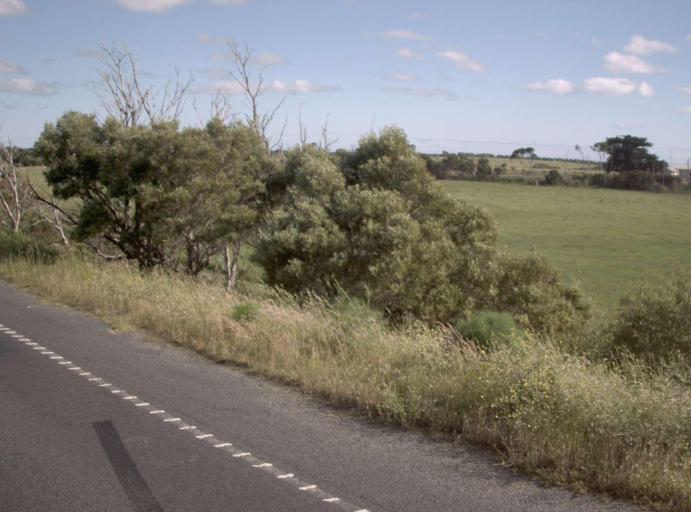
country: AU
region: Victoria
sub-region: Bass Coast
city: North Wonthaggi
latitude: -38.5674
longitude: 145.5623
